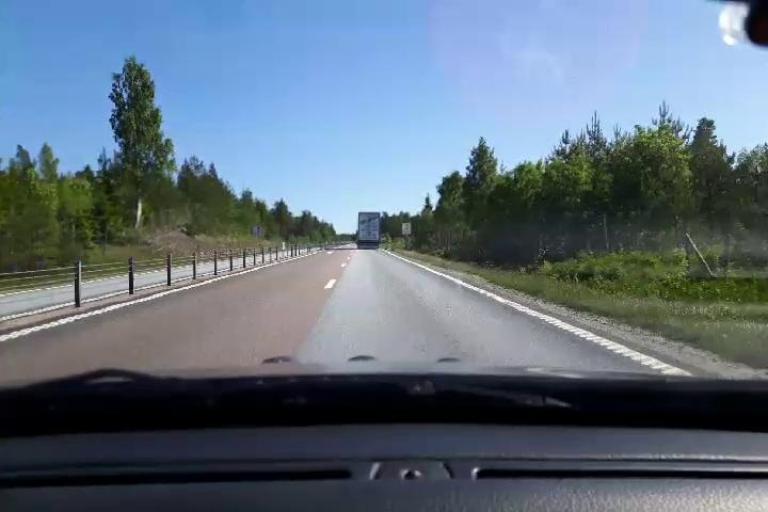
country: SE
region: Gaevleborg
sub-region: Soderhamns Kommun
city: Soderhamn
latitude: 61.2661
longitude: 17.0297
